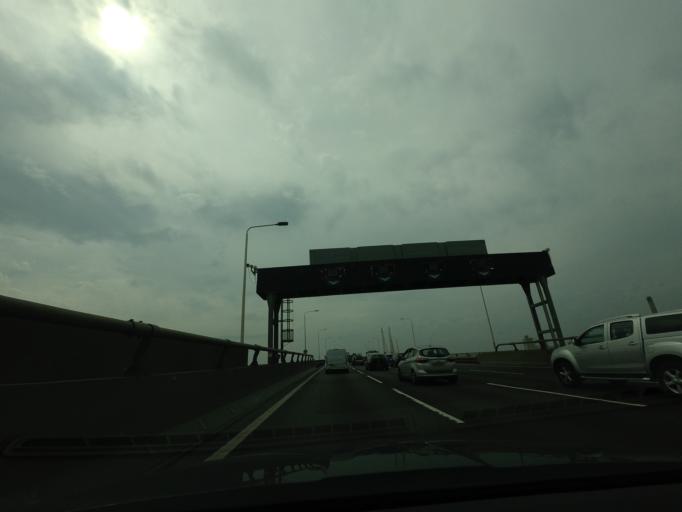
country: GB
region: England
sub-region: Kent
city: West Thurrock
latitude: 51.4739
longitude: 0.2660
